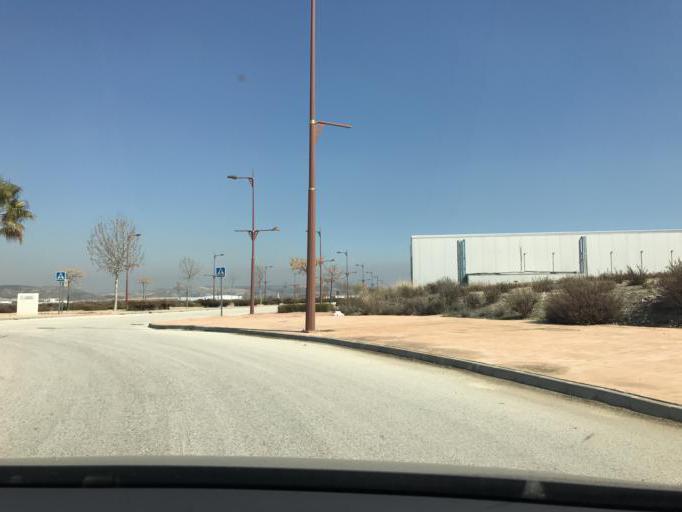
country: ES
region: Andalusia
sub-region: Provincia de Granada
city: Escuzar
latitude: 37.0723
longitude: -3.7674
